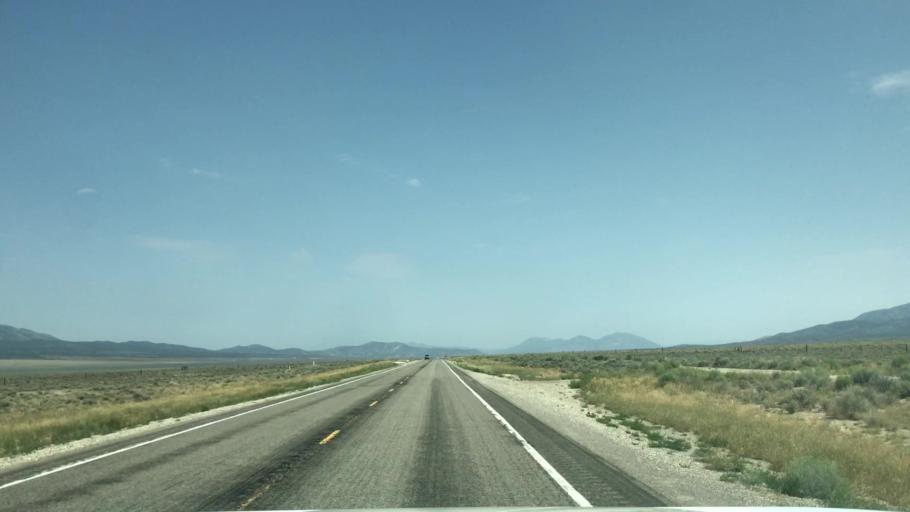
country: US
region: Nevada
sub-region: White Pine County
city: Ely
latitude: 39.0763
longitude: -114.7431
